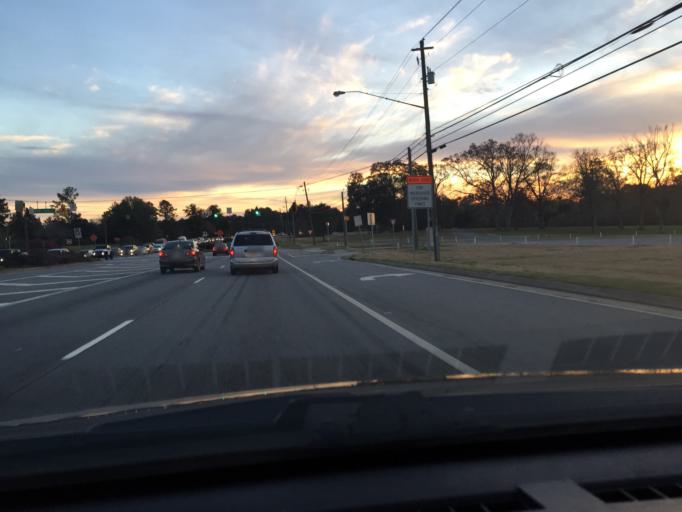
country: US
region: Georgia
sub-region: Gwinnett County
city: Berkeley Lake
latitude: 34.0059
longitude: -84.1940
